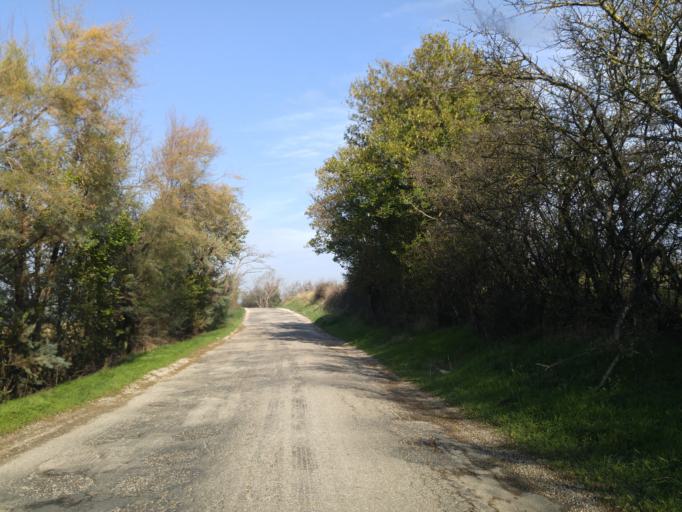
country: IT
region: The Marches
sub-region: Provincia di Pesaro e Urbino
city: Lucrezia
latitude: 43.8058
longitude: 12.9124
